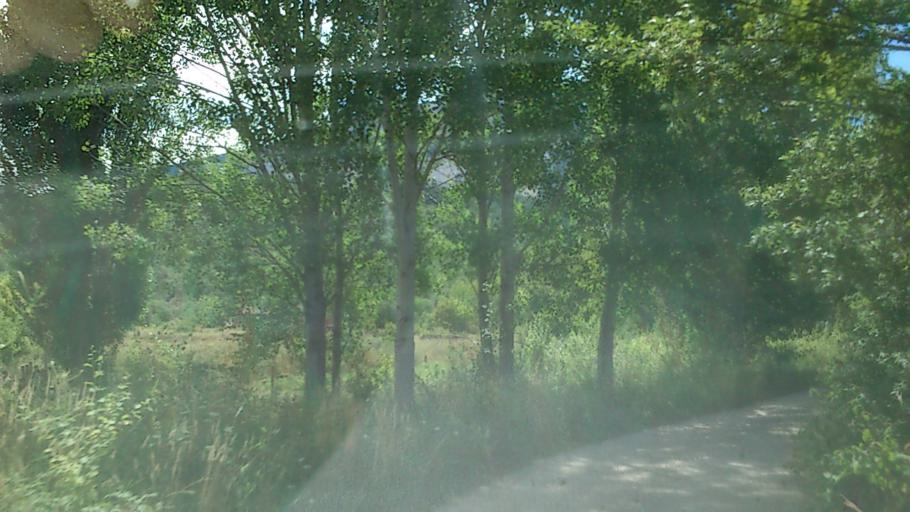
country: ES
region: Aragon
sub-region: Provincia de Huesca
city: Yebra de Basa
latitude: 42.3221
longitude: -0.2549
